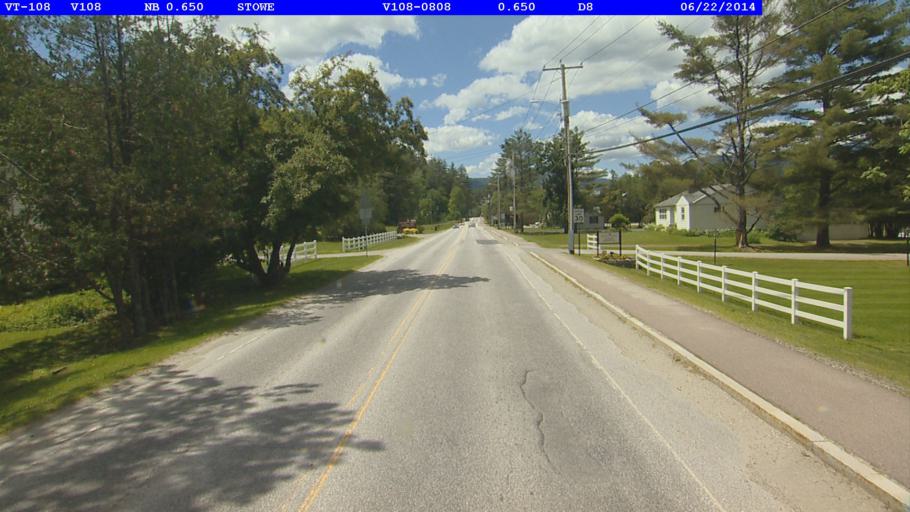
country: US
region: Vermont
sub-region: Lamoille County
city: Morristown
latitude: 44.4731
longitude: -72.6909
